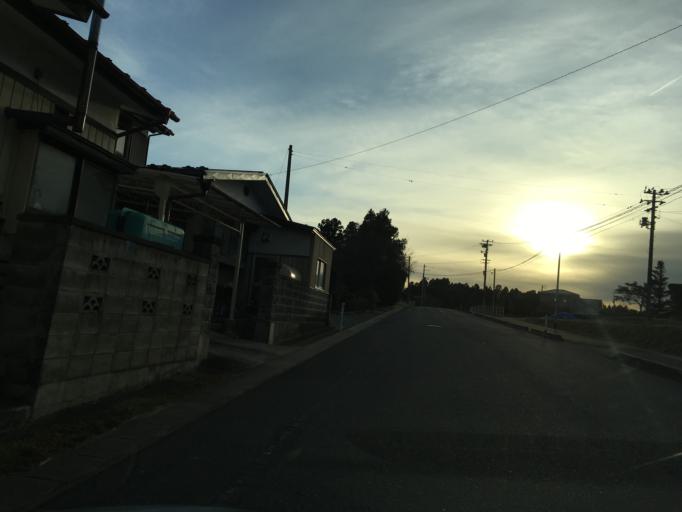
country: JP
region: Miyagi
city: Wakuya
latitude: 38.7058
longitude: 141.1184
